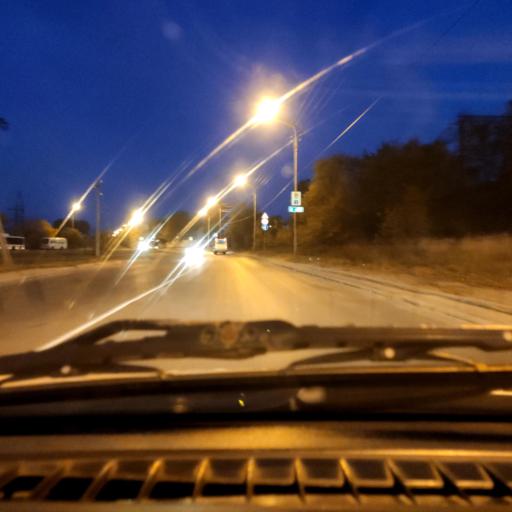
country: RU
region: Samara
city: Zhigulevsk
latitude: 53.4726
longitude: 49.5401
